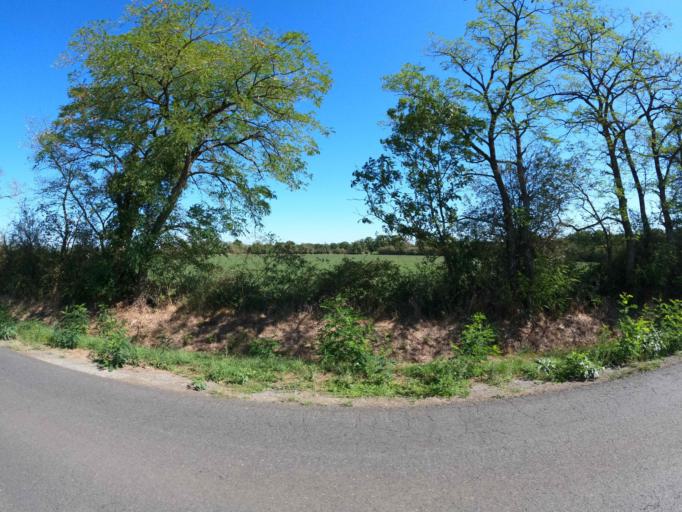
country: FR
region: Poitou-Charentes
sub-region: Departement de la Vienne
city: Lathus-Saint-Remy
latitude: 46.3580
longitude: 0.9445
